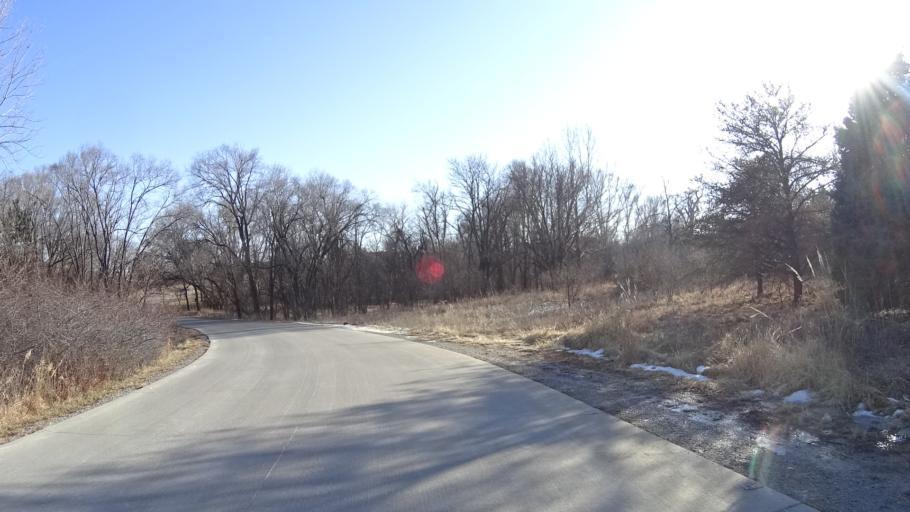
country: US
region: Nebraska
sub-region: Douglas County
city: Bennington
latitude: 41.3086
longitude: -96.1314
